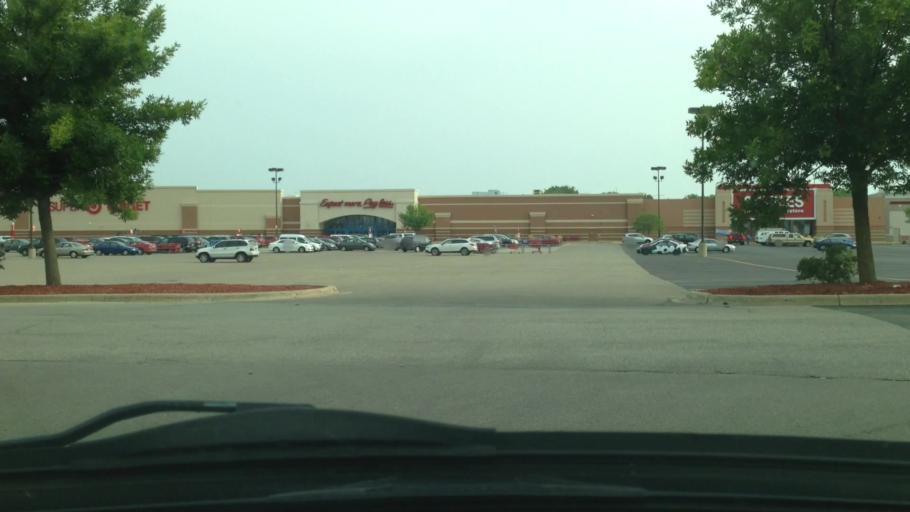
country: US
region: Minnesota
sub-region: Olmsted County
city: Rochester
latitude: 44.0648
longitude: -92.5046
